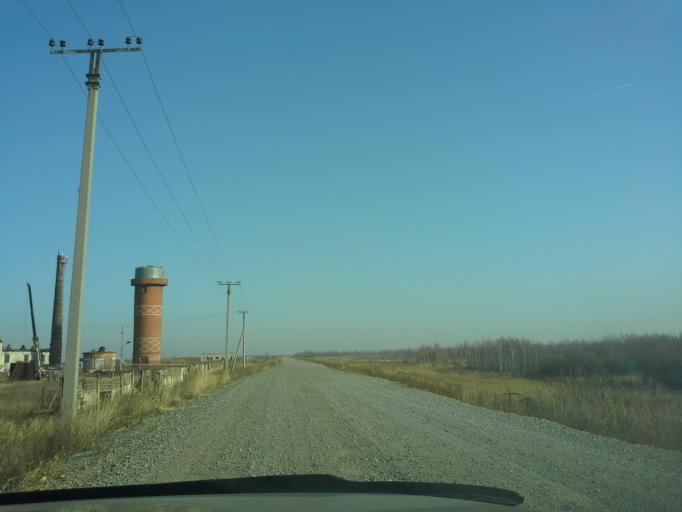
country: RU
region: Jewish Autonomous Oblast
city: Priamurskiy
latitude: 48.3579
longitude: 134.7958
